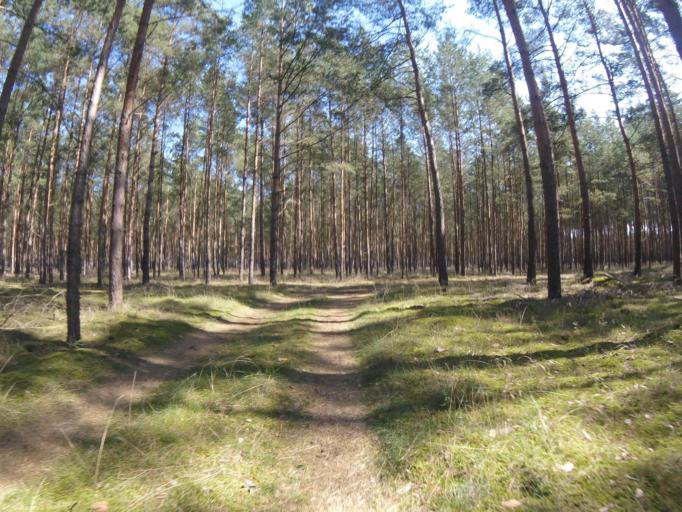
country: DE
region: Brandenburg
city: Mittenwalde
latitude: 52.2263
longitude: 13.5912
